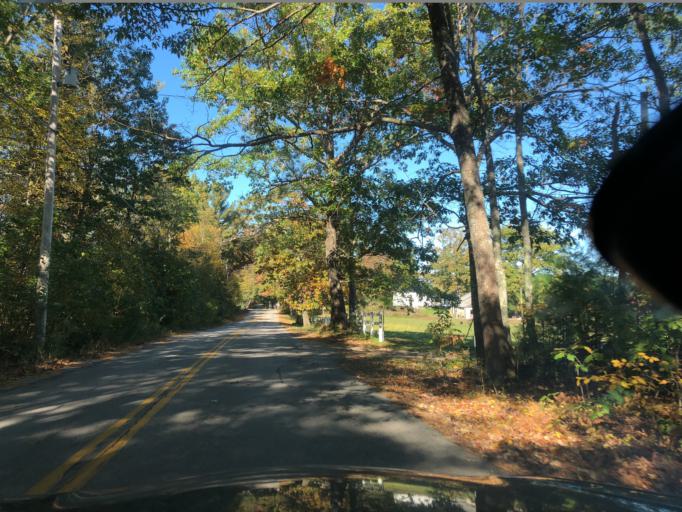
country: US
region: New Hampshire
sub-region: Strafford County
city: Lee
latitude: 43.1155
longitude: -70.9705
